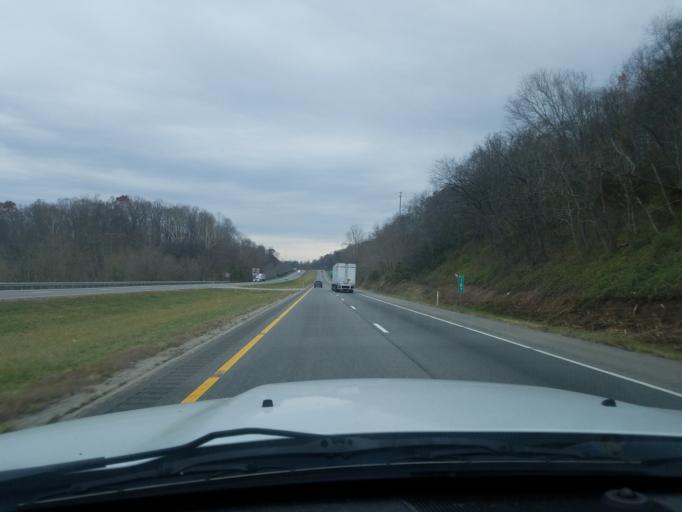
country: US
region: Kentucky
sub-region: Boyd County
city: Meads
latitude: 38.3761
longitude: -82.6722
